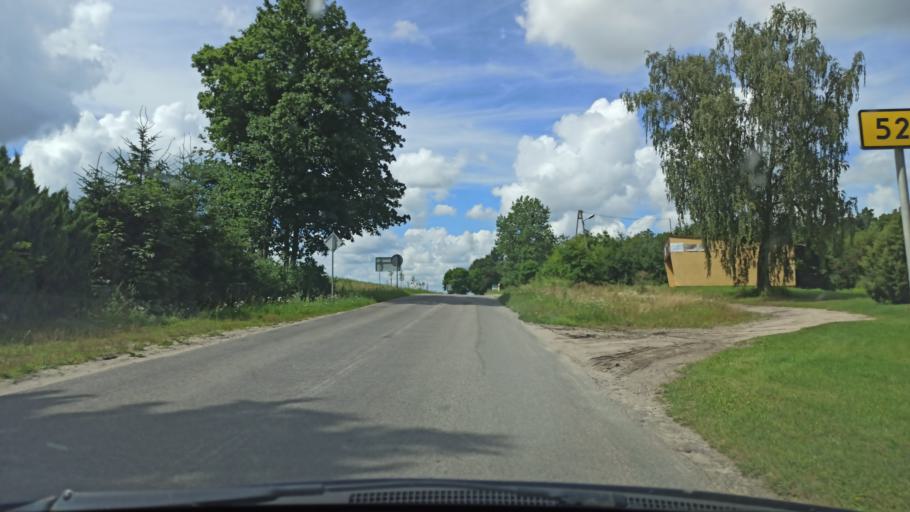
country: PL
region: Warmian-Masurian Voivodeship
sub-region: Powiat ostrodzki
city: Morag
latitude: 53.8562
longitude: 19.9810
